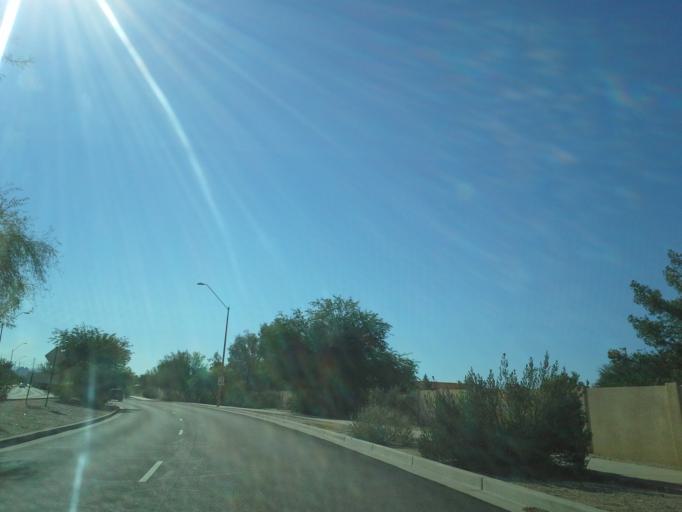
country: US
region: Arizona
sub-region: Maricopa County
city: Scottsdale
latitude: 33.6032
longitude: -111.8539
